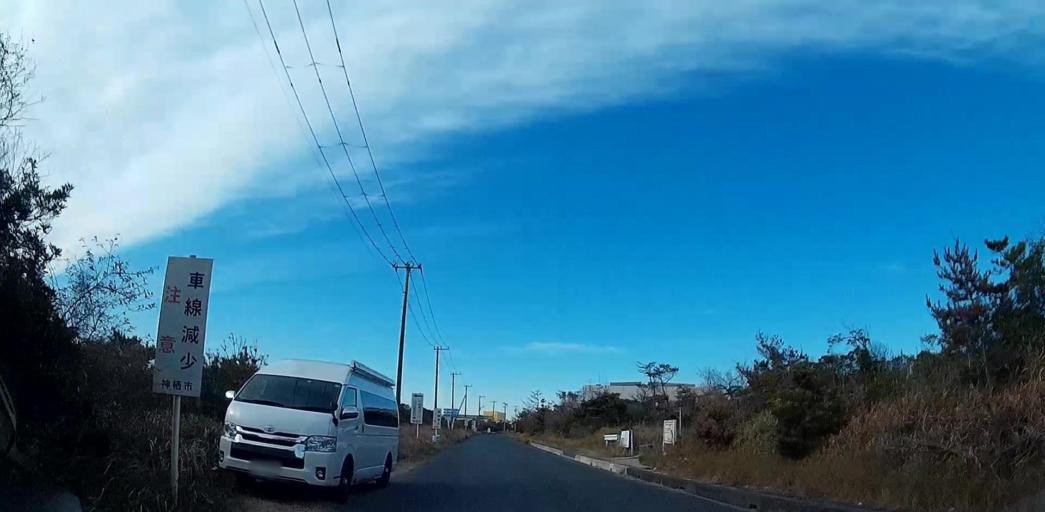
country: JP
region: Chiba
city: Hasaki
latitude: 35.7651
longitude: 140.8190
